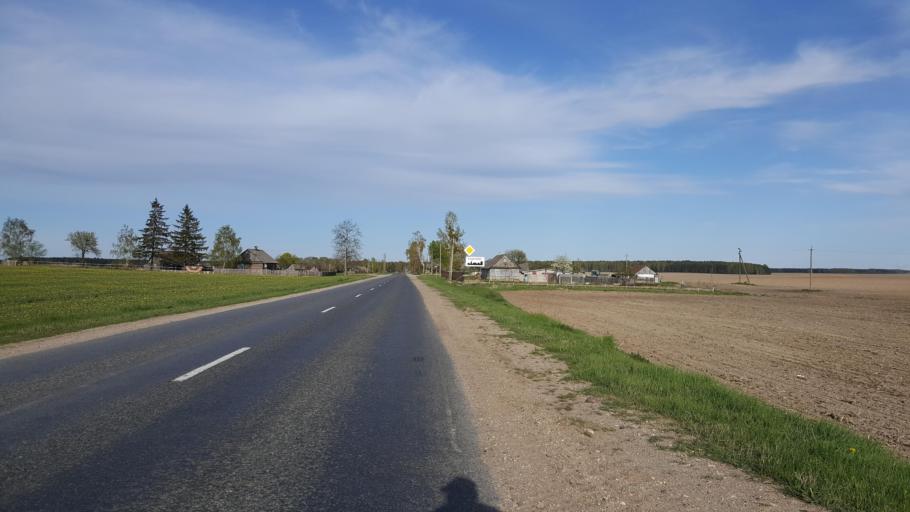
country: BY
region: Brest
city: Vysokaye
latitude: 52.4034
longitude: 23.5456
